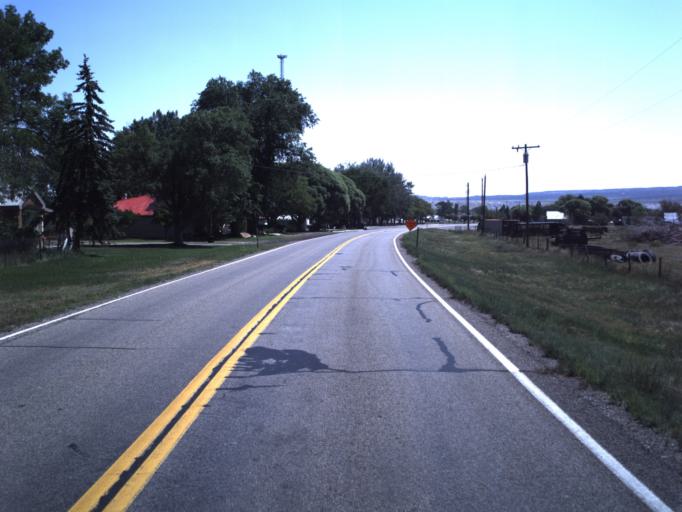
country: US
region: Utah
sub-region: Emery County
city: Ferron
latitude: 38.9227
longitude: -111.2548
